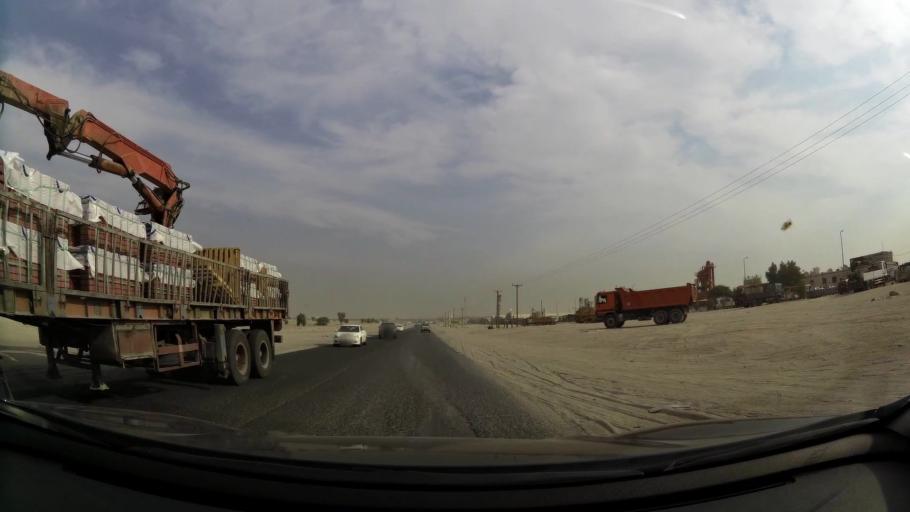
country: KW
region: Muhafazat al Jahra'
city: Al Jahra'
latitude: 29.3083
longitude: 47.7421
